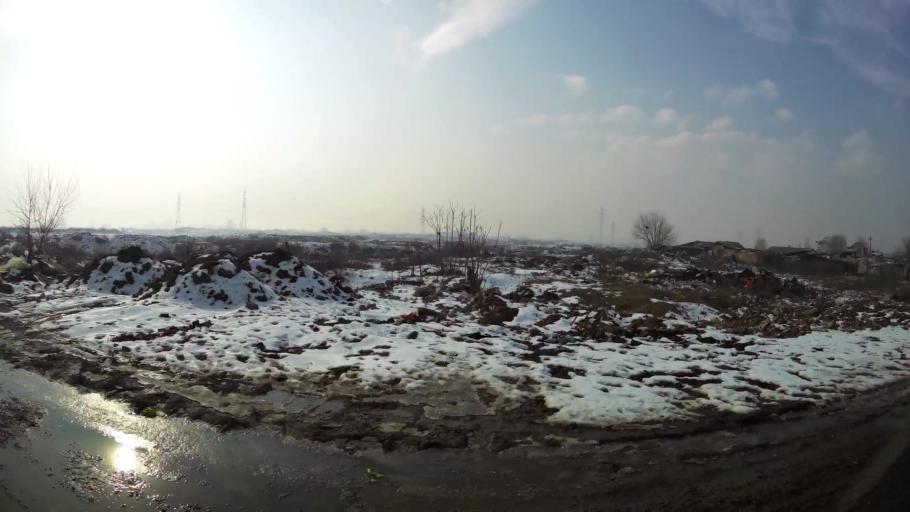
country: MK
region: Kisela Voda
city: Kisela Voda
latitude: 41.9856
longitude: 21.5007
